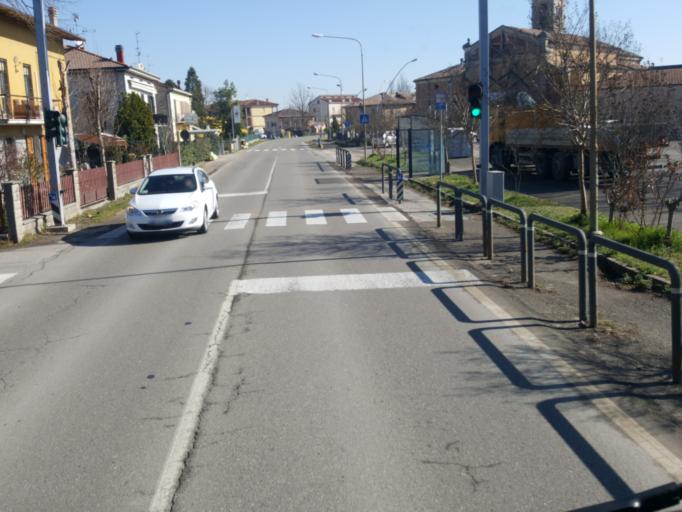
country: IT
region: Emilia-Romagna
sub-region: Provincia di Modena
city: Solara
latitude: 44.7721
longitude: 11.0735
